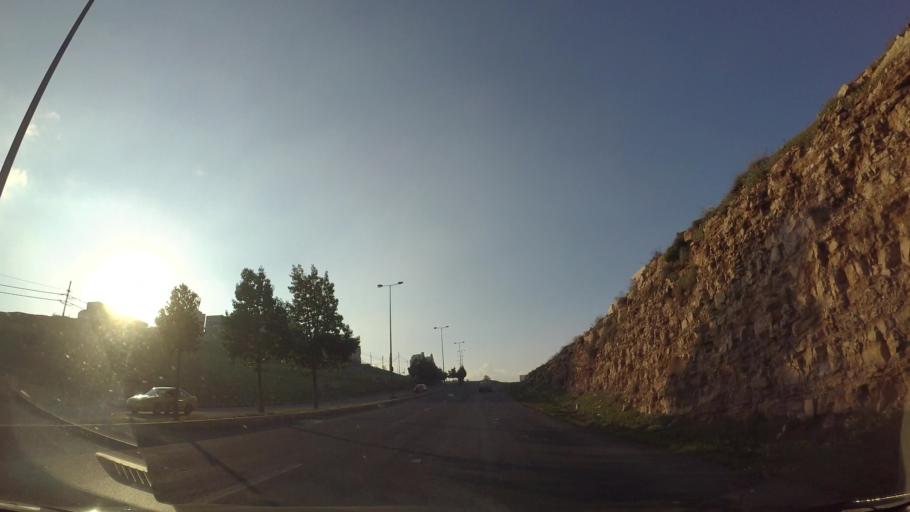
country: JO
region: Amman
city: Amman
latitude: 31.9833
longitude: 35.9579
